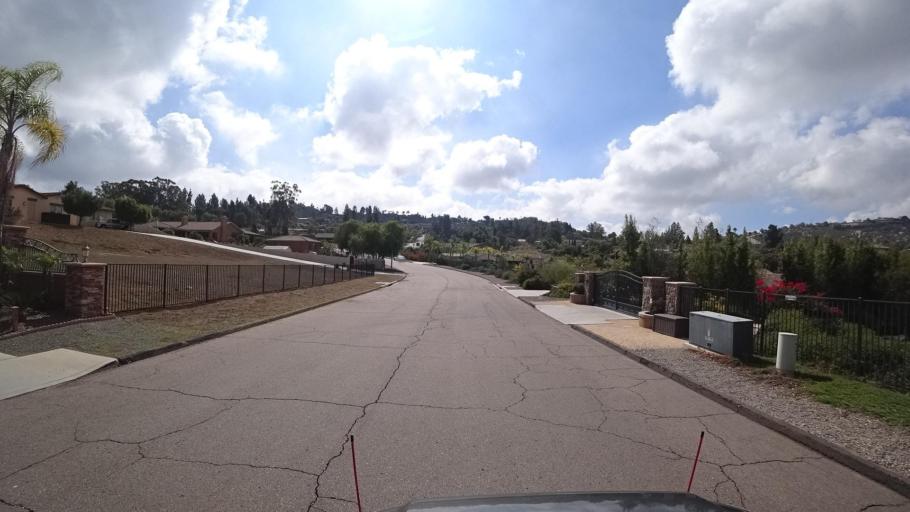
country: US
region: California
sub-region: San Diego County
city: Granite Hills
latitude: 32.7824
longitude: -116.9030
